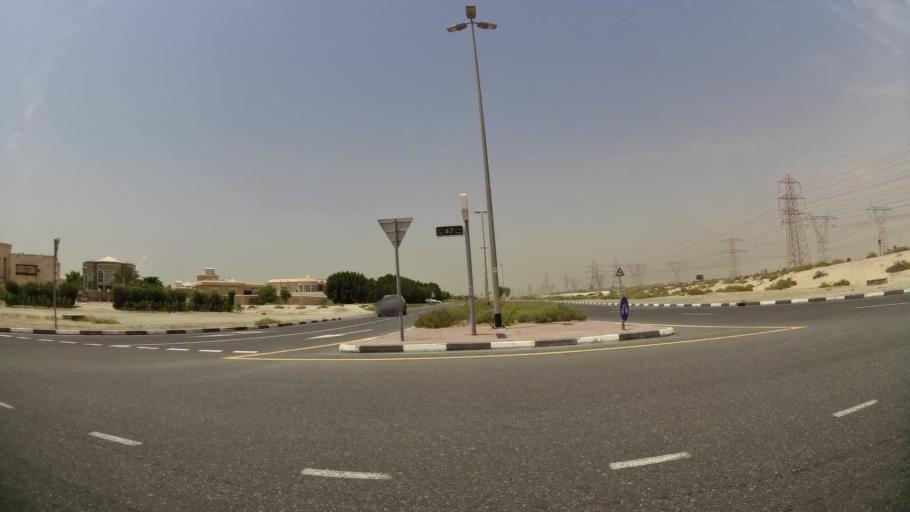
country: AE
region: Ash Shariqah
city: Sharjah
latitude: 25.1997
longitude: 55.3924
